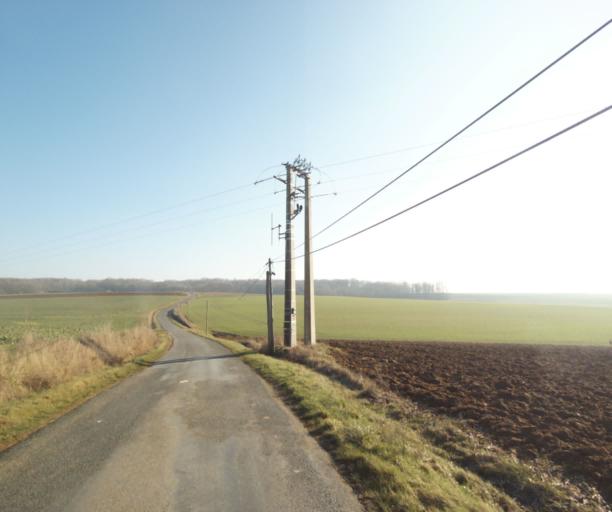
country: FR
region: Champagne-Ardenne
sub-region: Departement de la Haute-Marne
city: Wassy
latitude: 48.5101
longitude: 5.0172
